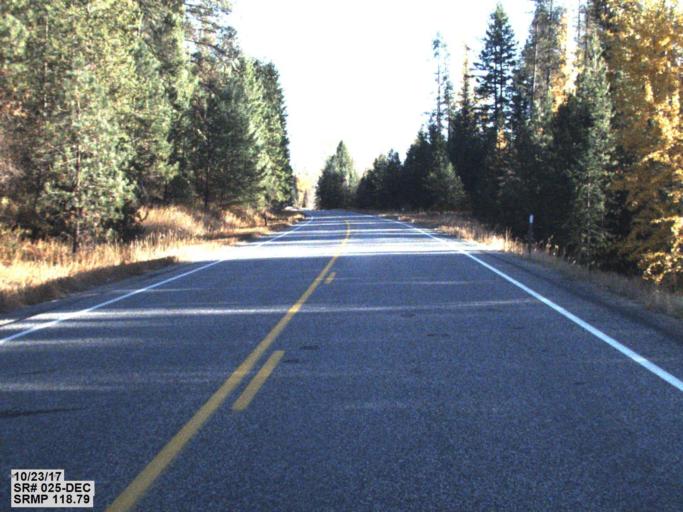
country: CA
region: British Columbia
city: Rossland
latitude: 48.9692
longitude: -117.8118
